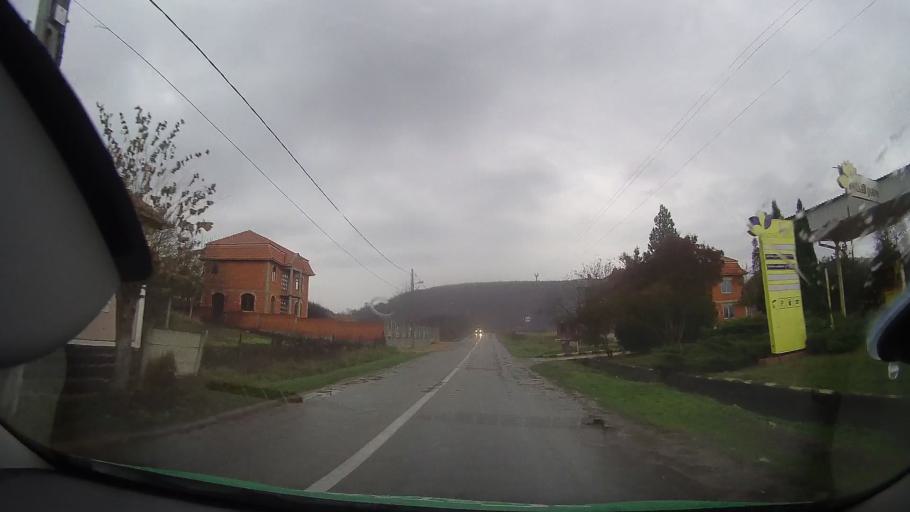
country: RO
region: Bihor
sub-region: Comuna Soimi
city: Soimi
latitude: 46.6836
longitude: 22.1129
